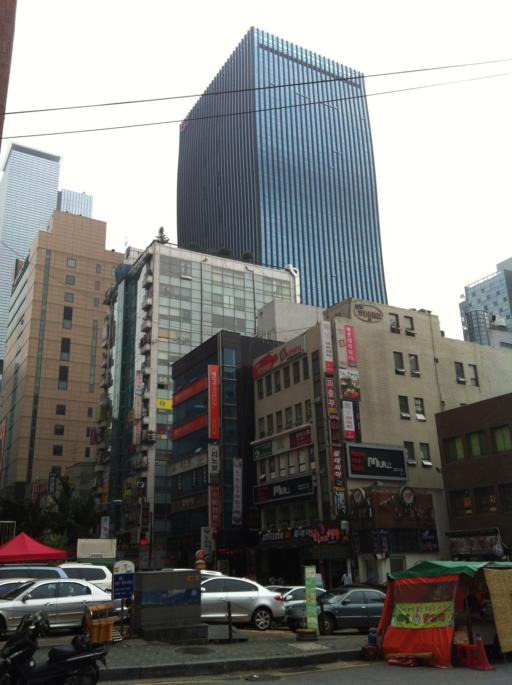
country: KR
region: Seoul
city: Seoul
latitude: 37.4994
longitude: 127.0262
